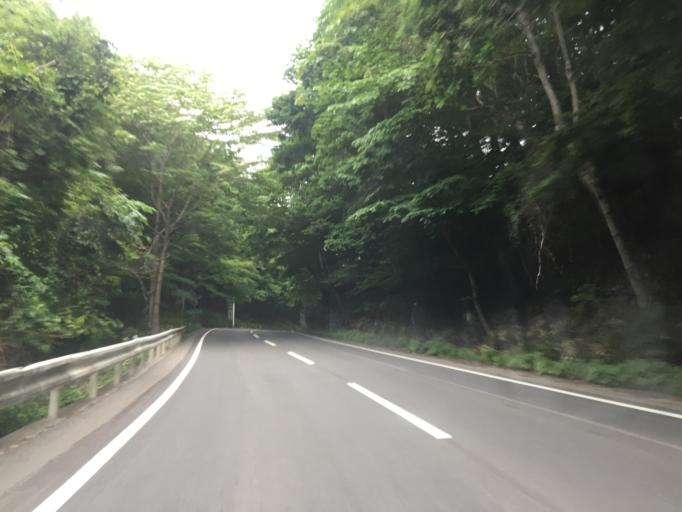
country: JP
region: Fukushima
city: Namie
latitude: 37.4064
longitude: 140.8600
